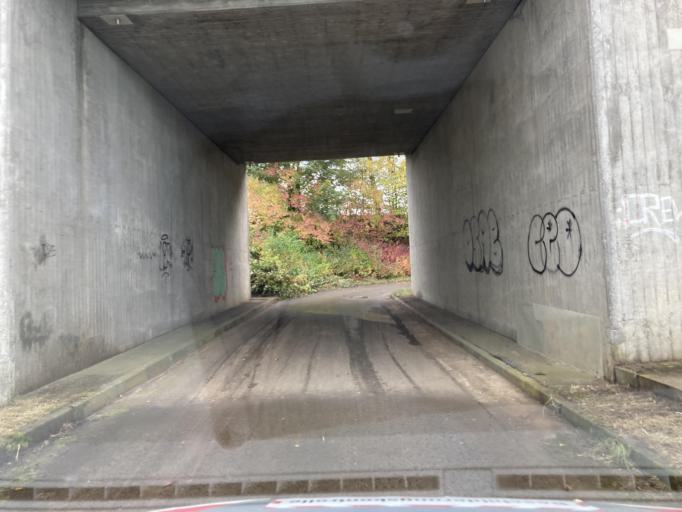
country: DE
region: Baden-Wuerttemberg
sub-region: Regierungsbezirk Stuttgart
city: Bondorf
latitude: 48.4992
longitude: 8.8611
